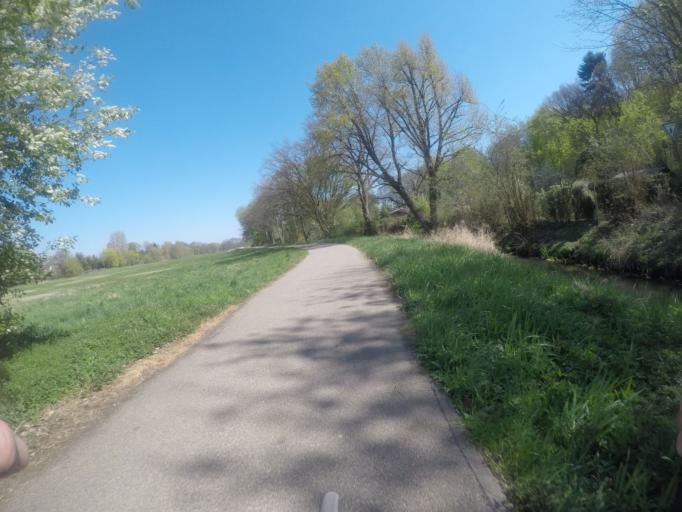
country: DE
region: Berlin
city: Buch
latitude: 52.6411
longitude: 13.5040
